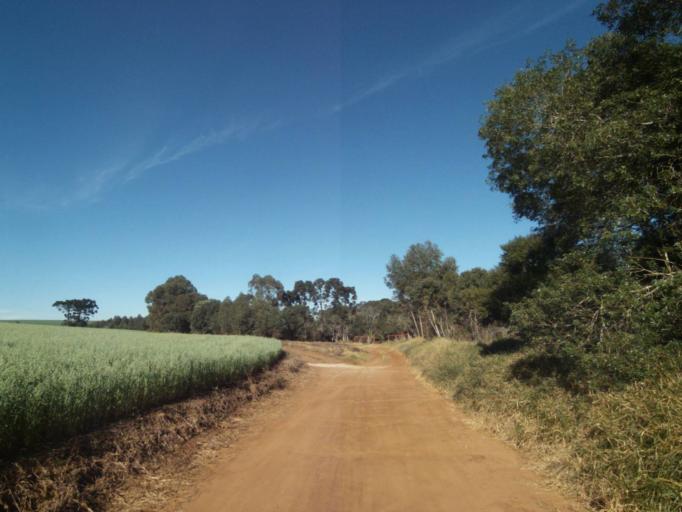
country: BR
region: Parana
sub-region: Tibagi
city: Tibagi
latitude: -24.5470
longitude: -50.3680
